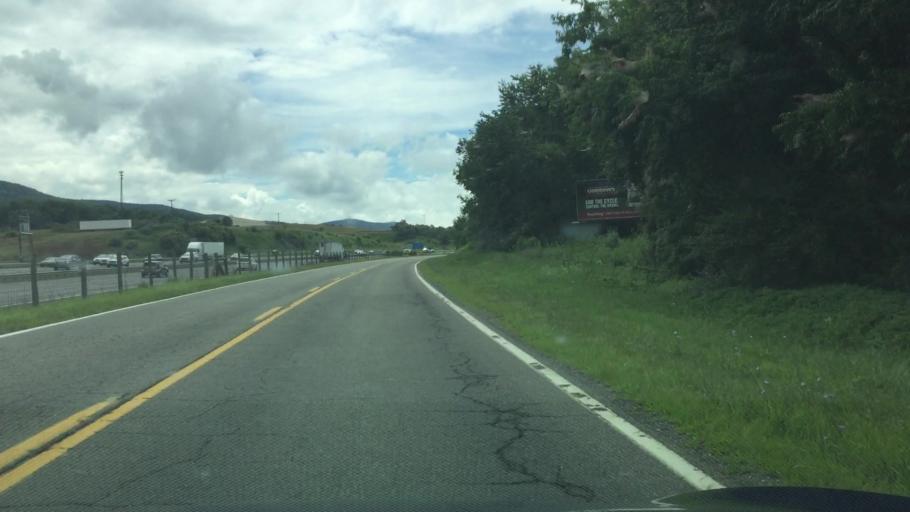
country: US
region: Virginia
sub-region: Wythe County
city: Wytheville
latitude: 36.9388
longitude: -80.9806
